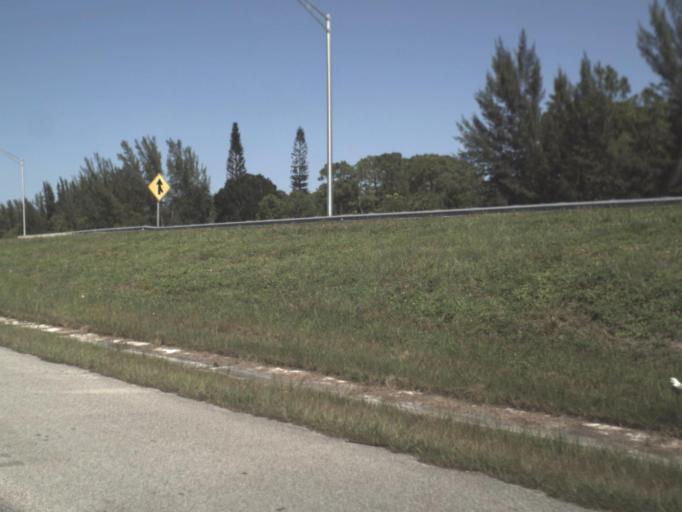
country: US
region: Florida
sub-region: Collier County
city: Golden Gate
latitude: 26.1759
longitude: -81.7347
